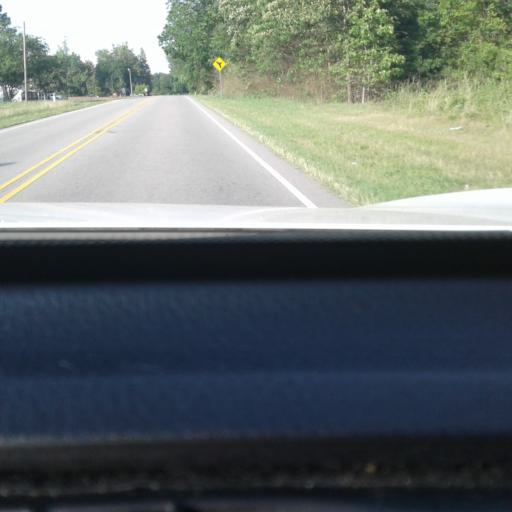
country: US
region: North Carolina
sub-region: Harnett County
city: Dunn
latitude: 35.3416
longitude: -78.5843
